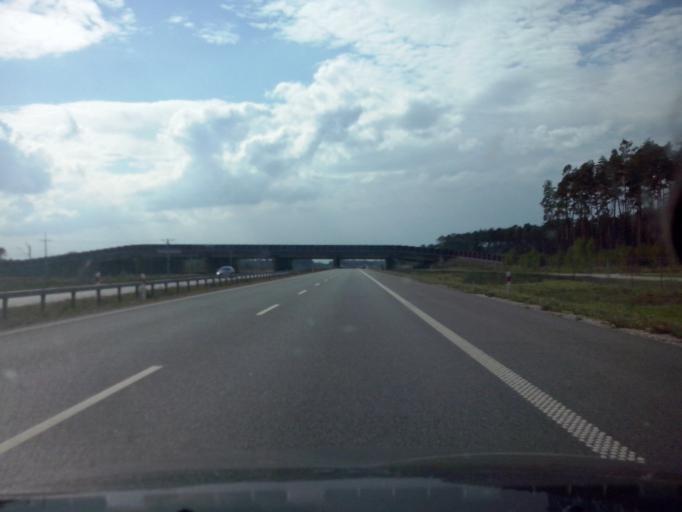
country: PL
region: Lesser Poland Voivodeship
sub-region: Powiat tarnowski
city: Wierzchoslawice
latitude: 50.0064
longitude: 20.7954
